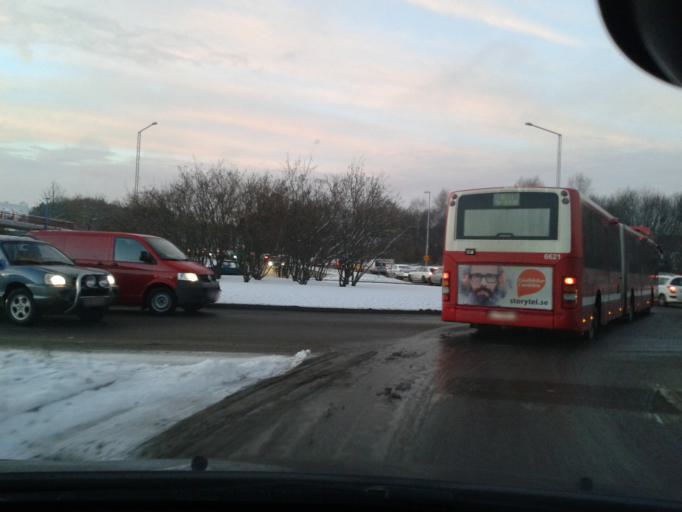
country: SE
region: Stockholm
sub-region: Haninge Kommun
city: Haninge
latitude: 59.1795
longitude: 18.1632
